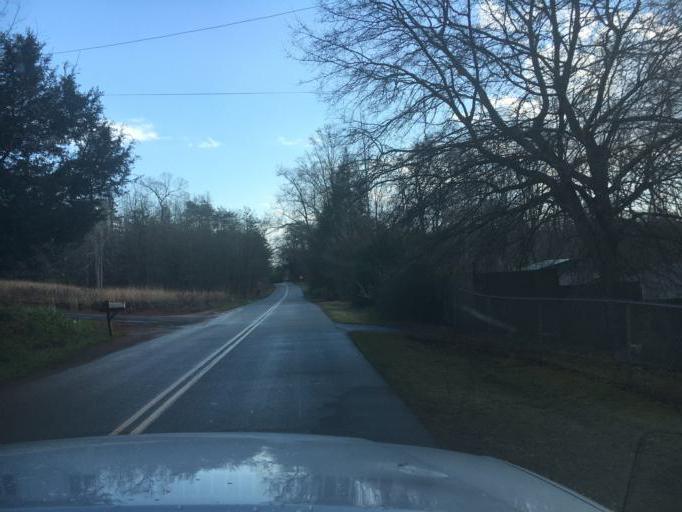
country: US
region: South Carolina
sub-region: Greenville County
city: Parker
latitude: 34.8605
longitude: -82.5019
